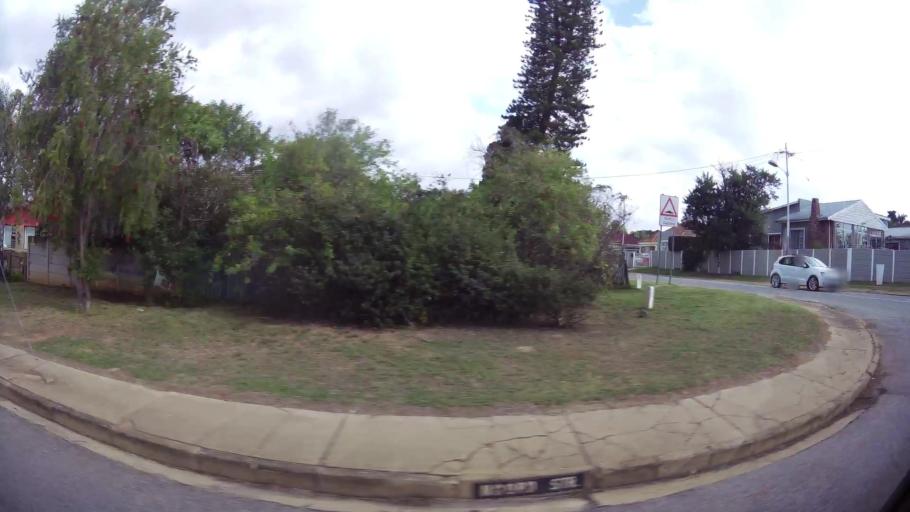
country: ZA
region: Eastern Cape
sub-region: Nelson Mandela Bay Metropolitan Municipality
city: Uitenhage
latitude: -33.7520
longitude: 25.4096
